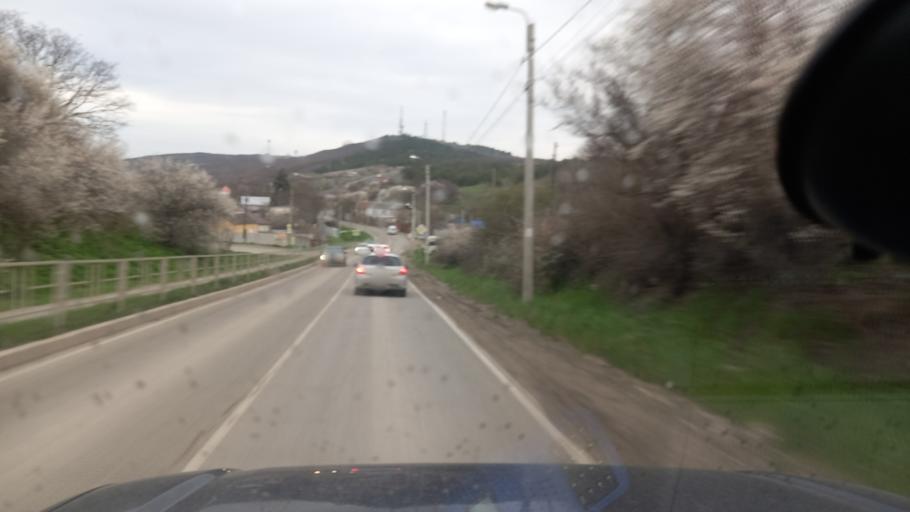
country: RU
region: Krasnodarskiy
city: Anapskaya
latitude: 44.8437
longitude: 37.3843
